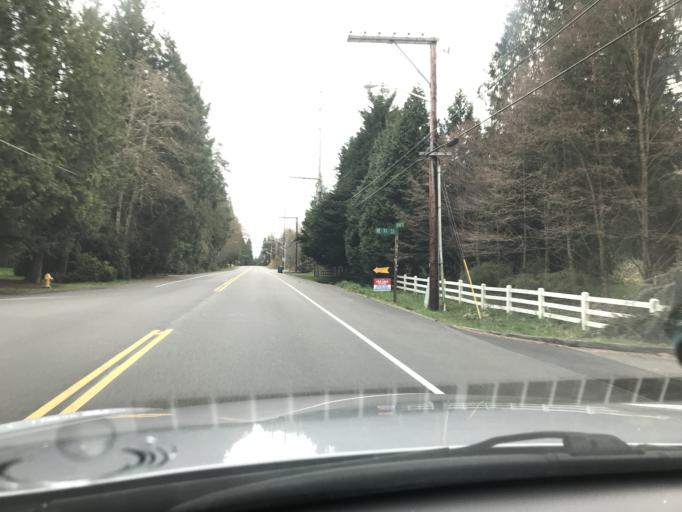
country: US
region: Washington
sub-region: King County
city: Union Hill-Novelty Hill
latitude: 47.6828
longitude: -122.0627
